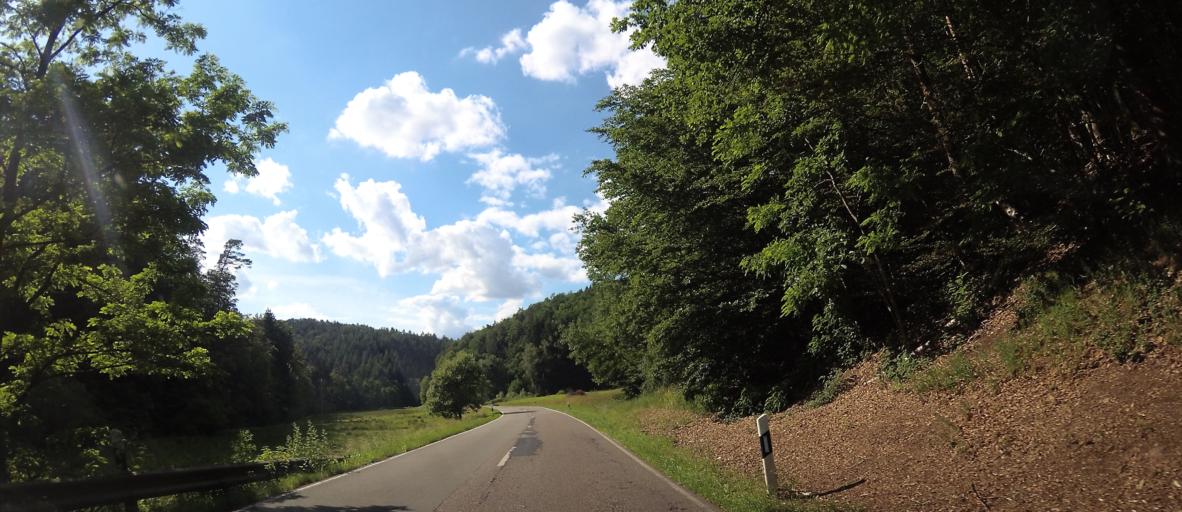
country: DE
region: Rheinland-Pfalz
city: Trulben
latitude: 49.1174
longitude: 7.5496
